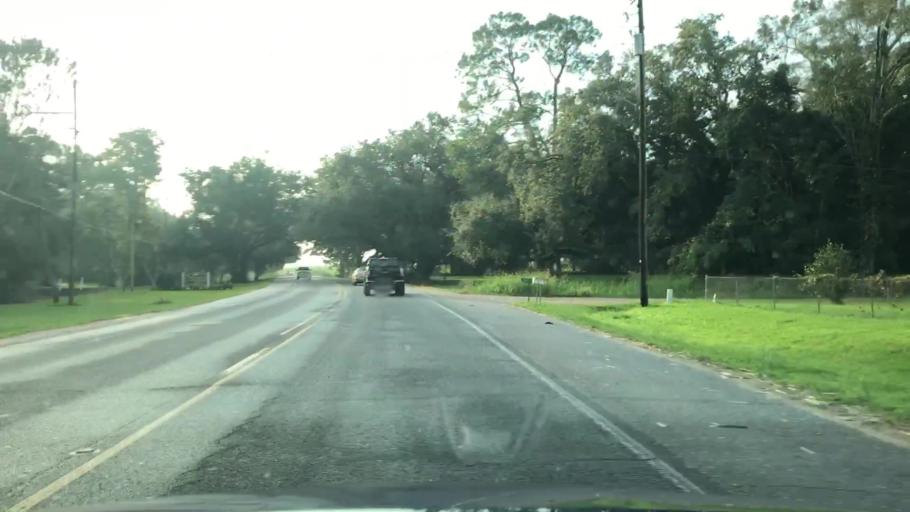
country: US
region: Louisiana
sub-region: Terrebonne Parish
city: Bayou Cane
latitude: 29.6326
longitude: -90.8086
